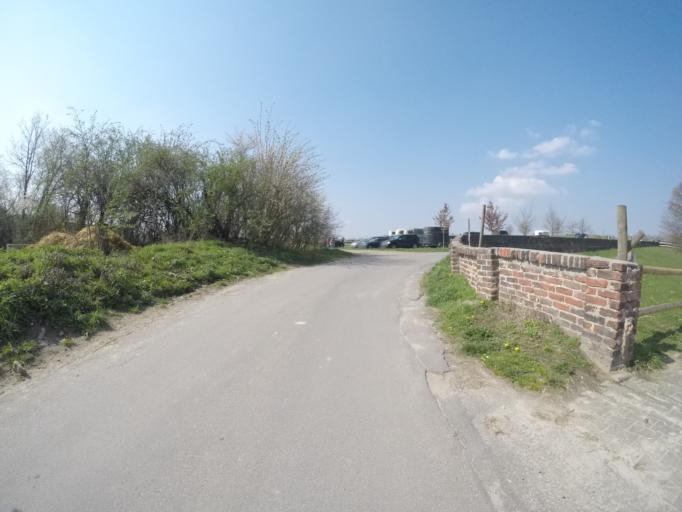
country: DE
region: North Rhine-Westphalia
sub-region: Regierungsbezirk Detmold
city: Bielefeld
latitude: 52.0585
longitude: 8.5867
